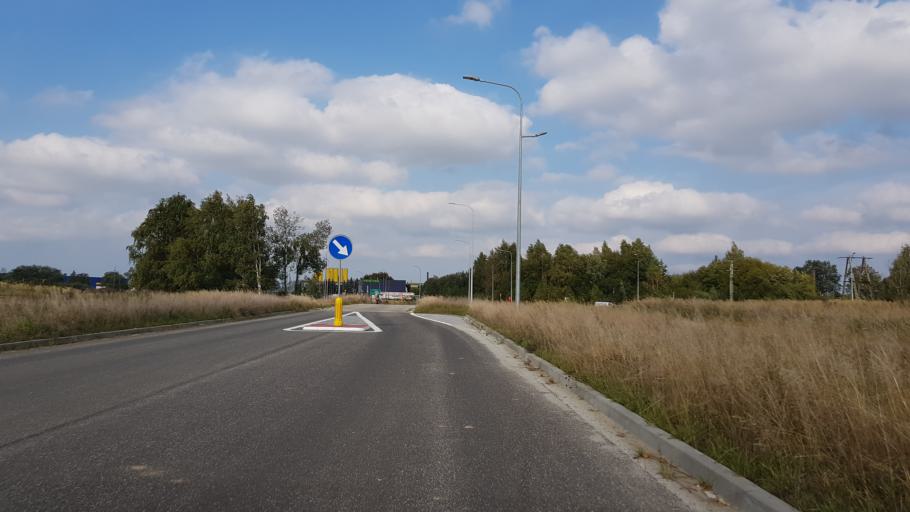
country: PL
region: West Pomeranian Voivodeship
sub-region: Koszalin
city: Koszalin
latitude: 54.1799
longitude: 16.1537
